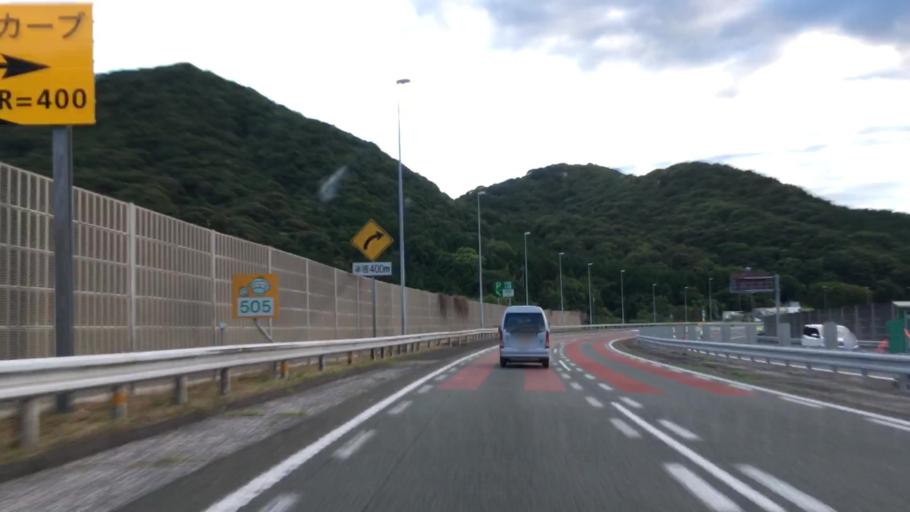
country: JP
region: Yamaguchi
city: Onoda
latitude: 34.1207
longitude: 131.2105
